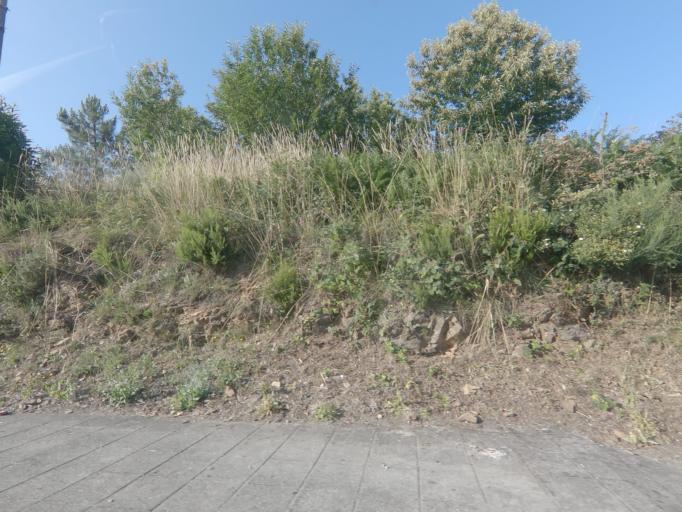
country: PT
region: Vila Real
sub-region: Vila Real
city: Vila Real
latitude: 41.2911
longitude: -7.7364
